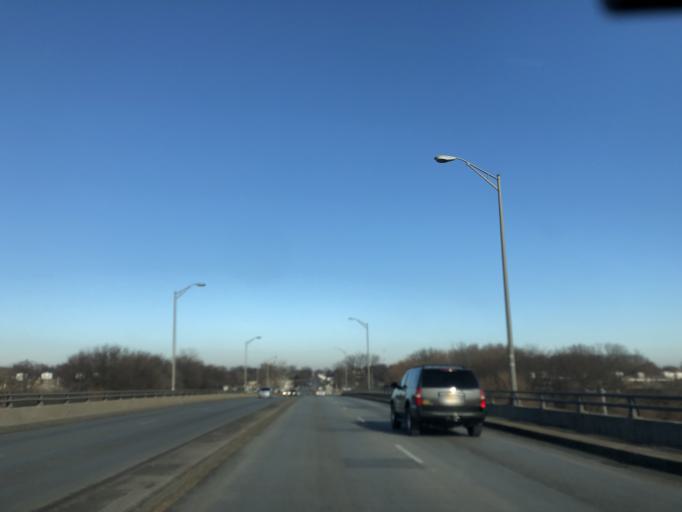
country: US
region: Illinois
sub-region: Cook County
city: Stickney
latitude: 41.8186
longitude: -87.7629
